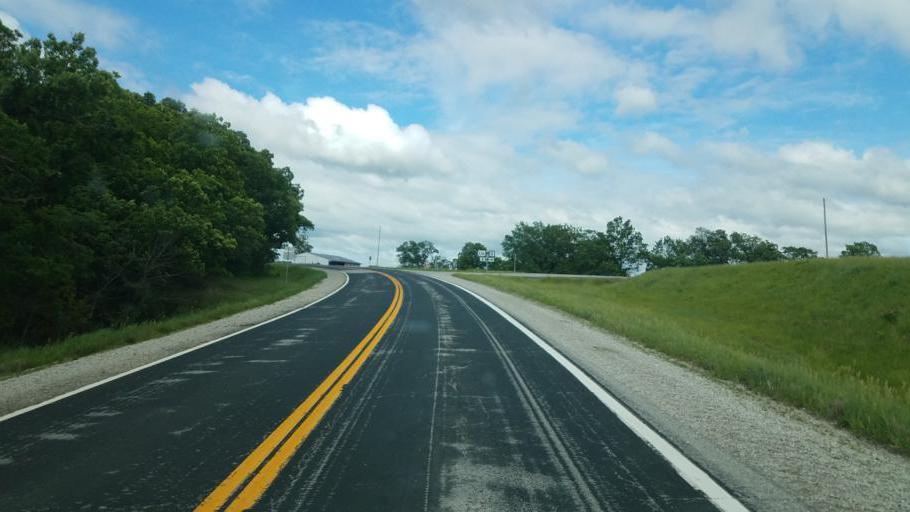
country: US
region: Missouri
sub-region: Mercer County
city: Princeton
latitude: 40.3398
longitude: -93.7481
